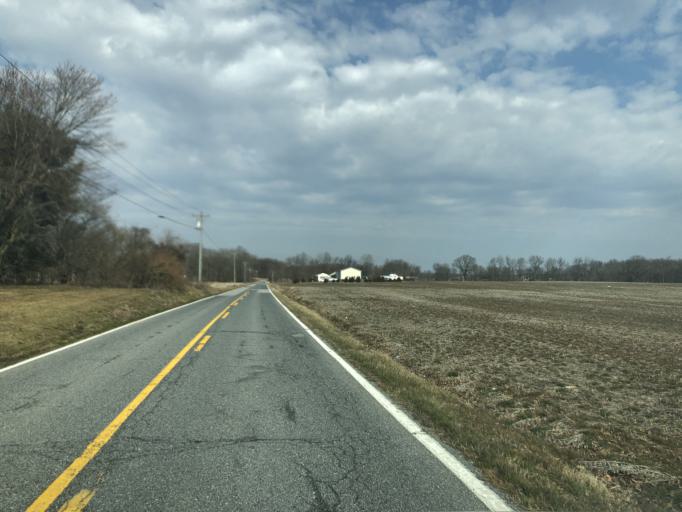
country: US
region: Maryland
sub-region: Caroline County
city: Ridgely
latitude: 39.0687
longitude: -75.9296
